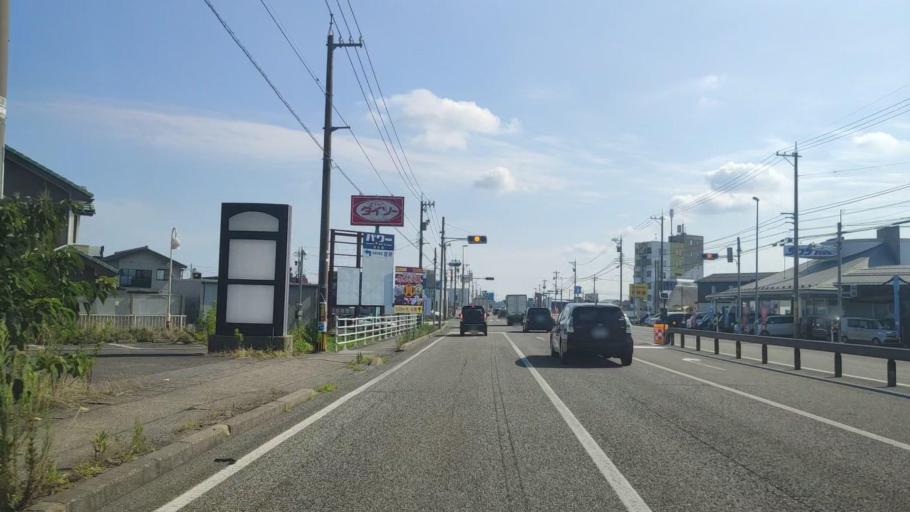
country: JP
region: Ishikawa
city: Matsuto
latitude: 36.5203
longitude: 136.5793
